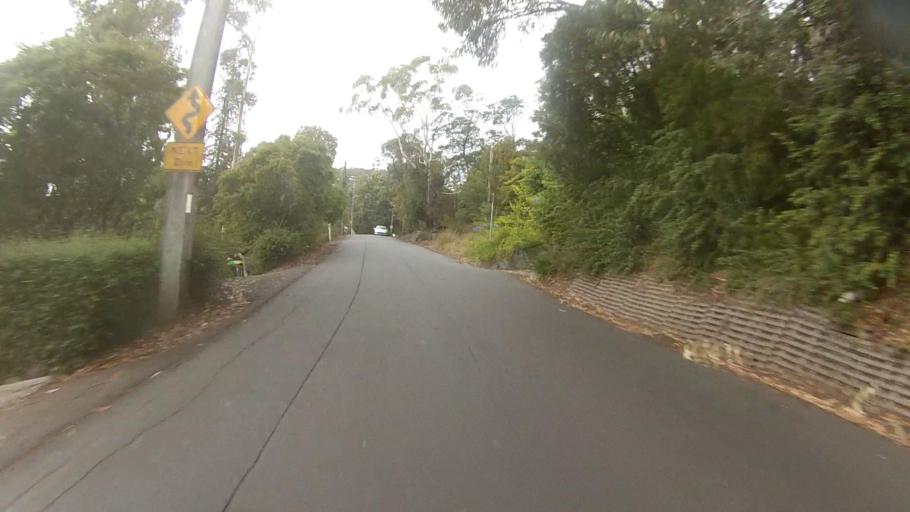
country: AU
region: Tasmania
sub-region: Hobart
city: Dynnyrne
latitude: -42.9093
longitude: 147.3289
